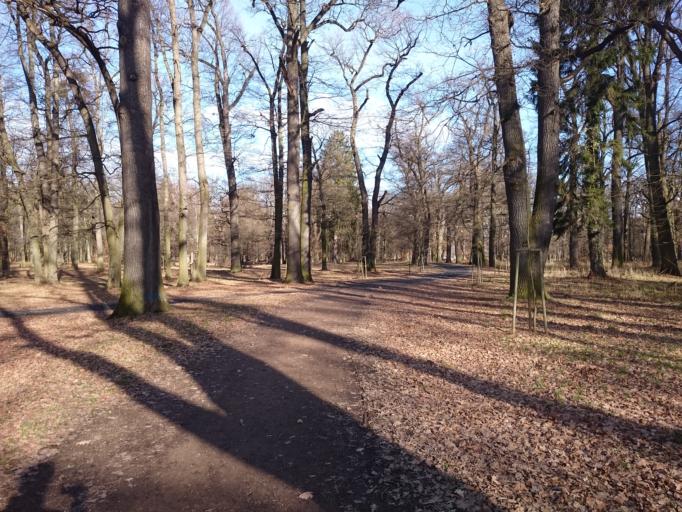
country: CZ
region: Pardubicky
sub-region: Okres Chrudim
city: Hermanuv Mestec
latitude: 49.9475
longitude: 15.6773
